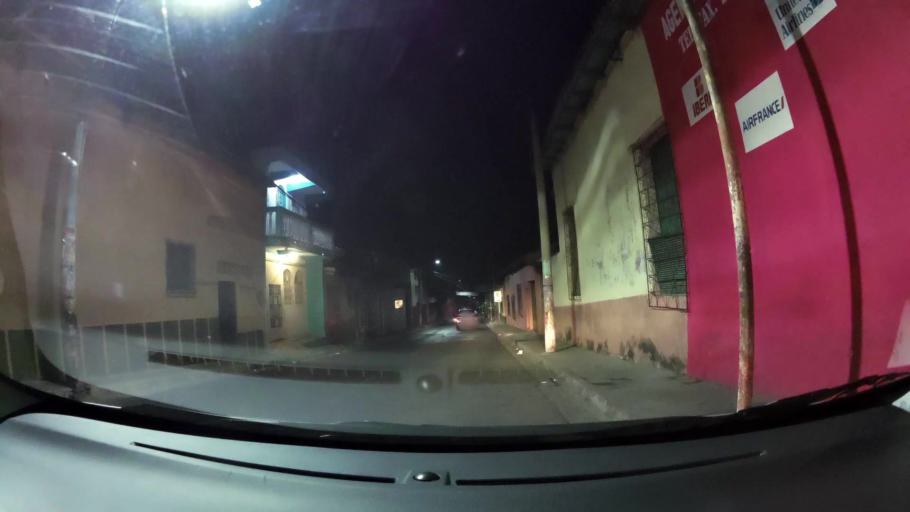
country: SV
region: La Paz
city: Zacatecoluca
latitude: 13.5072
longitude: -88.8712
